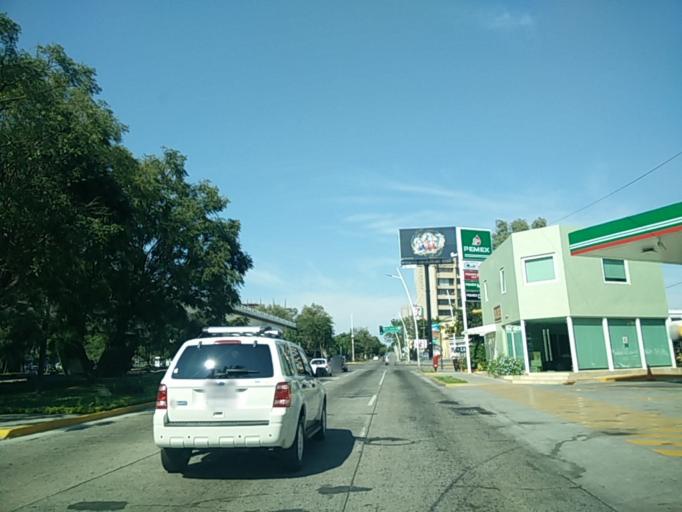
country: MX
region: Jalisco
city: Guadalajara
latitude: 20.6659
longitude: -103.3952
